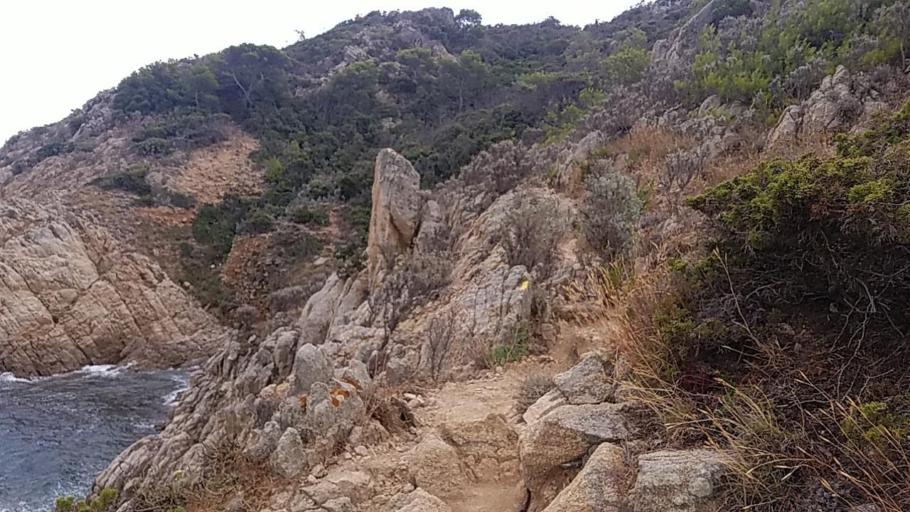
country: FR
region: Provence-Alpes-Cote d'Azur
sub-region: Departement du Var
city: Ramatuelle
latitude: 43.2052
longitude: 6.6721
